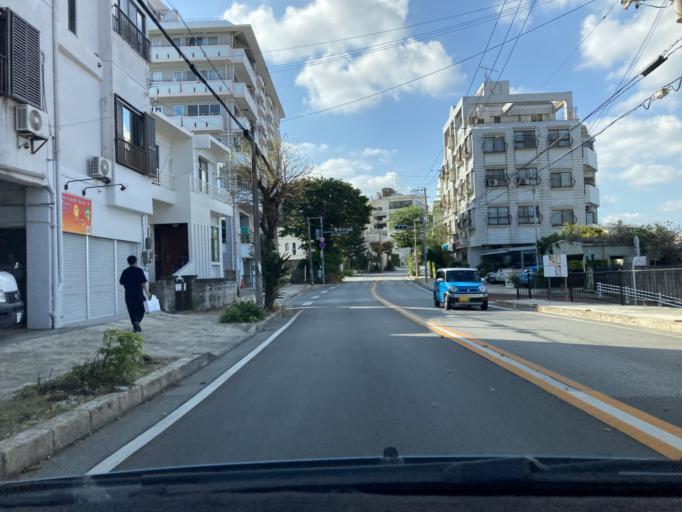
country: JP
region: Okinawa
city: Naha-shi
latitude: 26.2224
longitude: 127.7133
